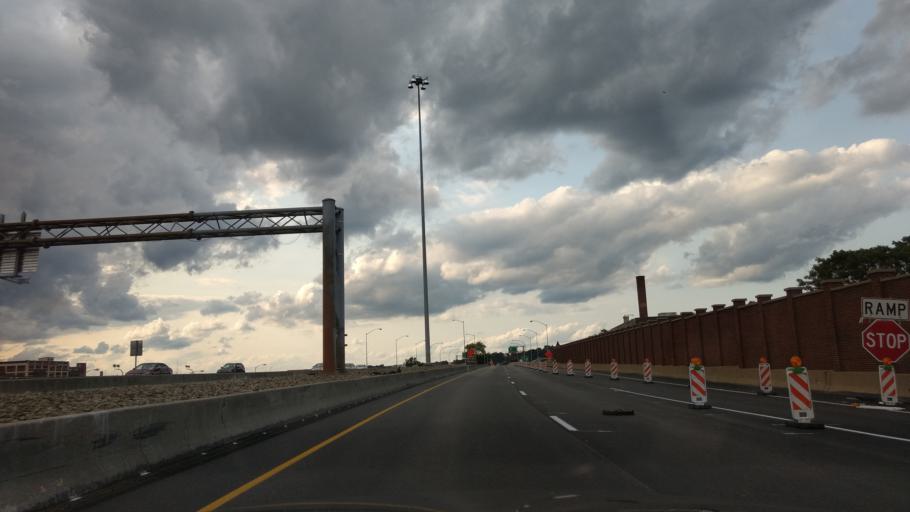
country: US
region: Pennsylvania
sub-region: Allegheny County
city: Pittsburgh
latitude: 40.4517
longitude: -80.0275
